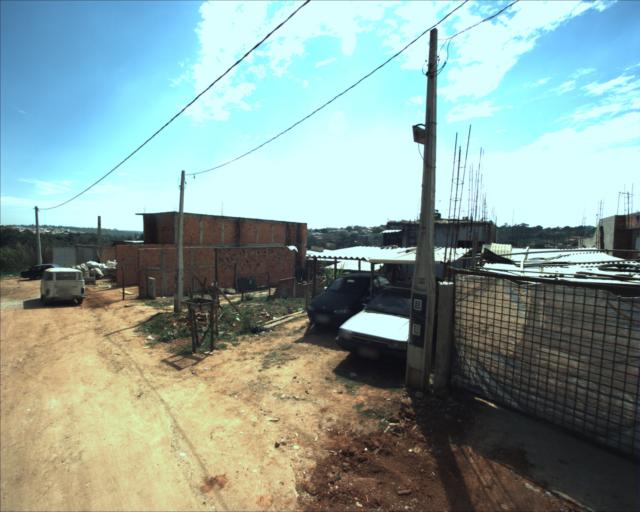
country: BR
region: Sao Paulo
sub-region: Sorocaba
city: Sorocaba
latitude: -23.4827
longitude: -47.5040
